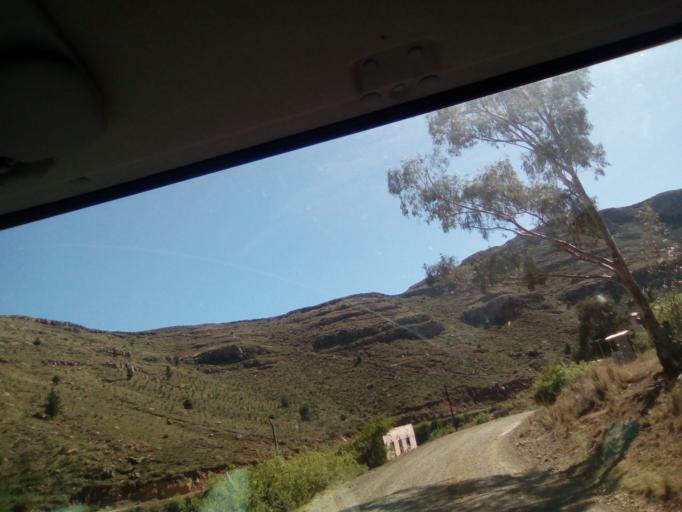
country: LS
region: Qacha's Nek
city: Qacha's Nek
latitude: -30.0595
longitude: 28.6378
